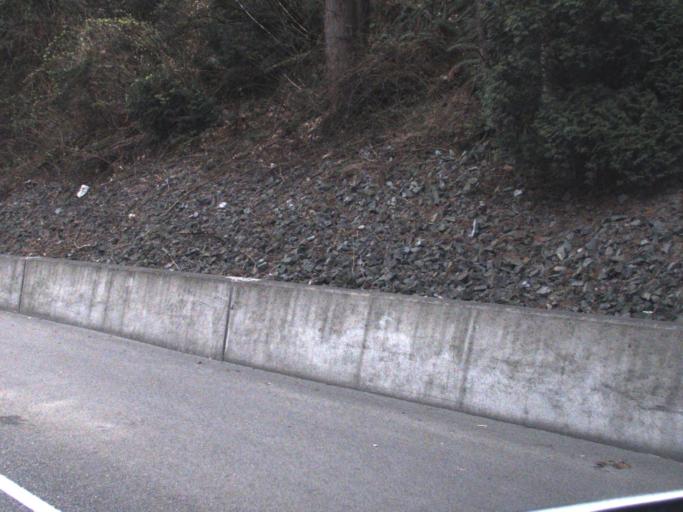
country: US
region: Washington
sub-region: King County
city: Lakeland South
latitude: 47.3012
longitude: -122.2788
